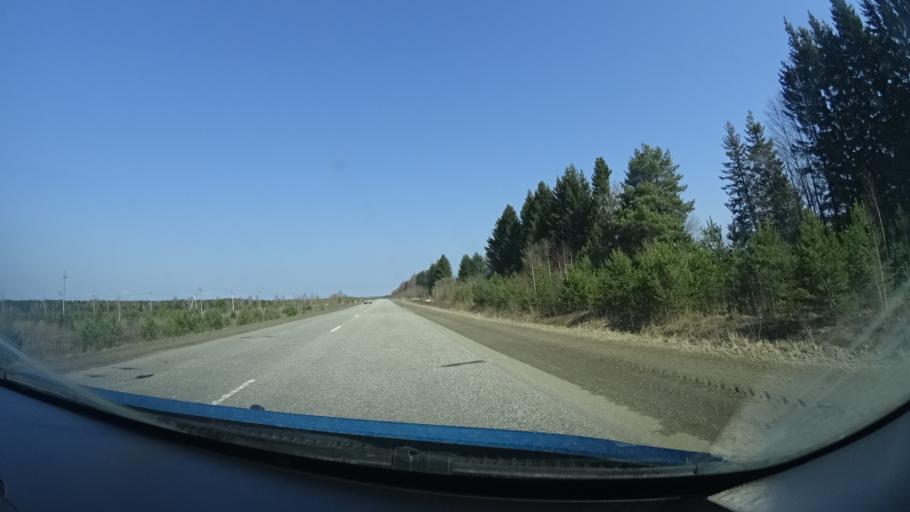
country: RU
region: Perm
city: Osa
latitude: 57.3387
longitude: 55.5866
